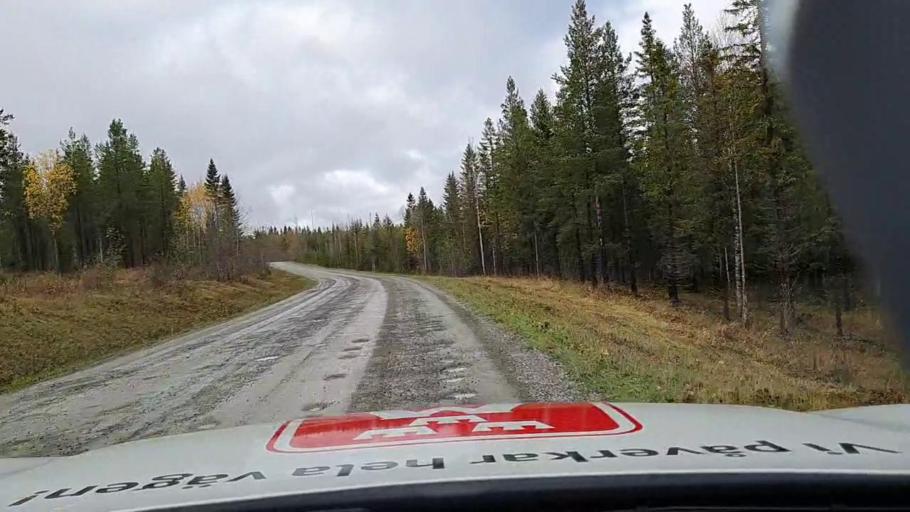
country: SE
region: Jaemtland
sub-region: Bergs Kommun
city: Hoverberg
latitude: 62.9975
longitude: 14.1518
